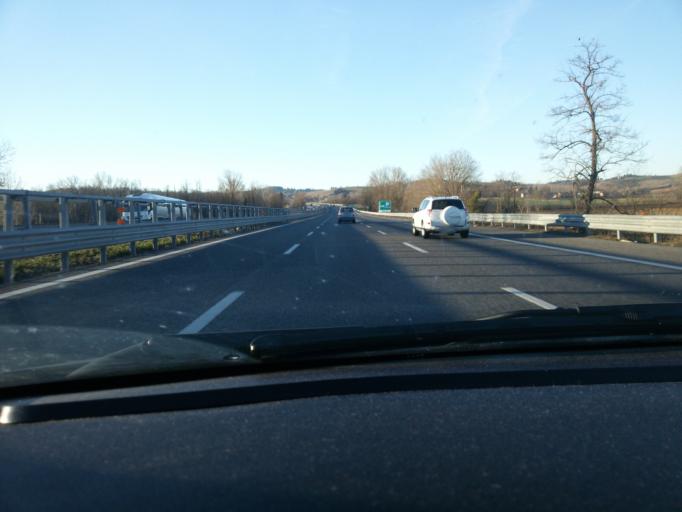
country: IT
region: Piedmont
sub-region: Provincia di Alessandria
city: Mirabello Monferrato
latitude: 45.0224
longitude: 8.5370
